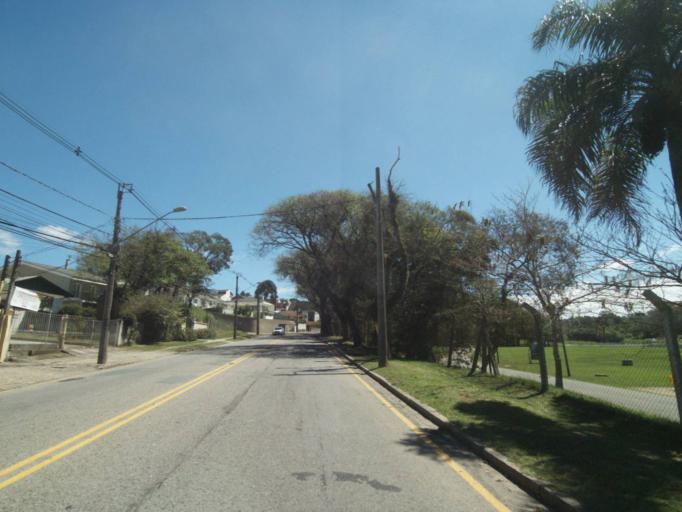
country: BR
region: Parana
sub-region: Curitiba
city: Curitiba
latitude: -25.3862
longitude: -49.2675
